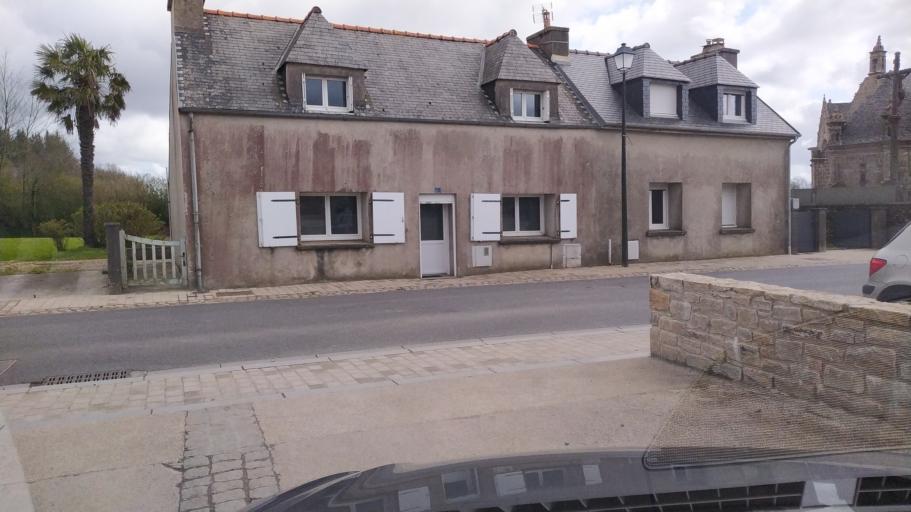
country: FR
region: Brittany
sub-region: Departement du Finistere
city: Bodilis
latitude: 48.5313
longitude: -4.1166
